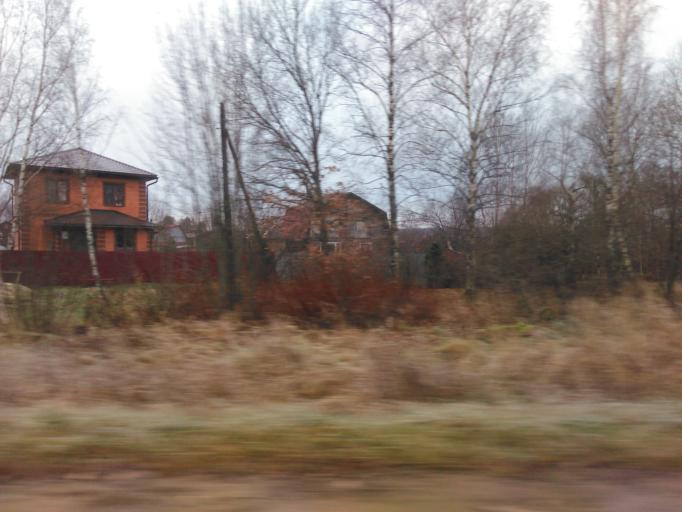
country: RU
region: Moskovskaya
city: Ashukino
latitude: 56.1758
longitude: 37.9382
